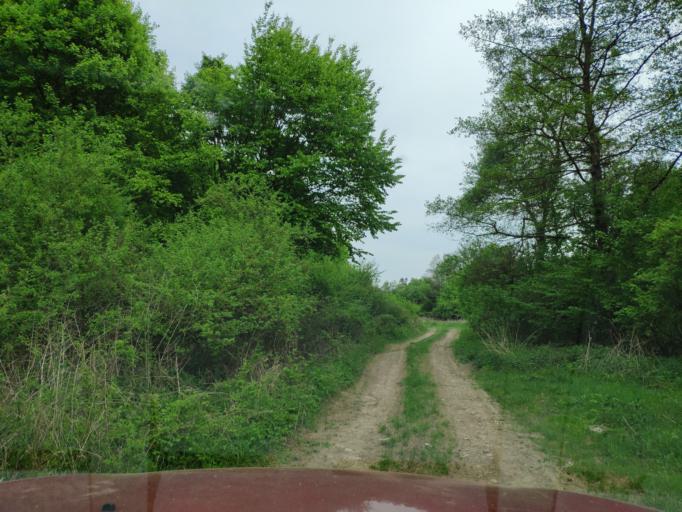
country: SK
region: Banskobystricky
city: Revuca
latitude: 48.5167
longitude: 20.1650
